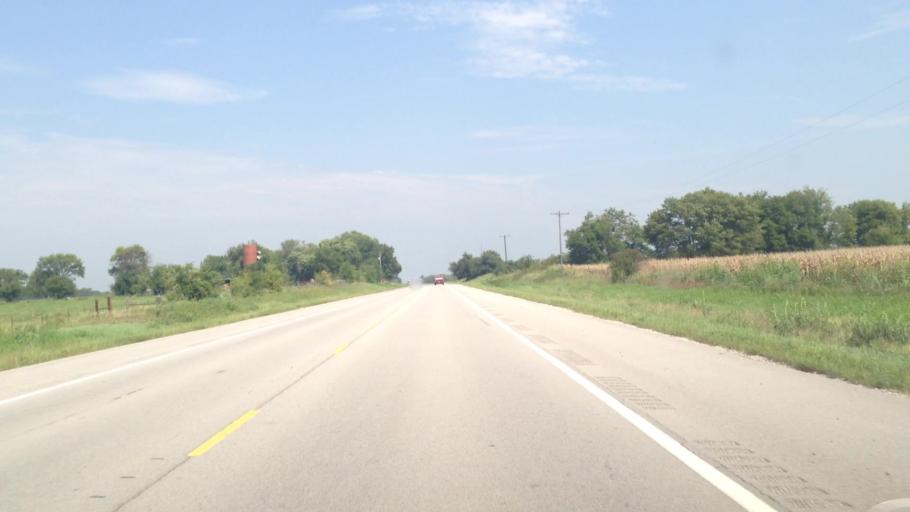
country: US
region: Kansas
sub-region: Labette County
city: Altamont
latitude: 37.2403
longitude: -95.2671
